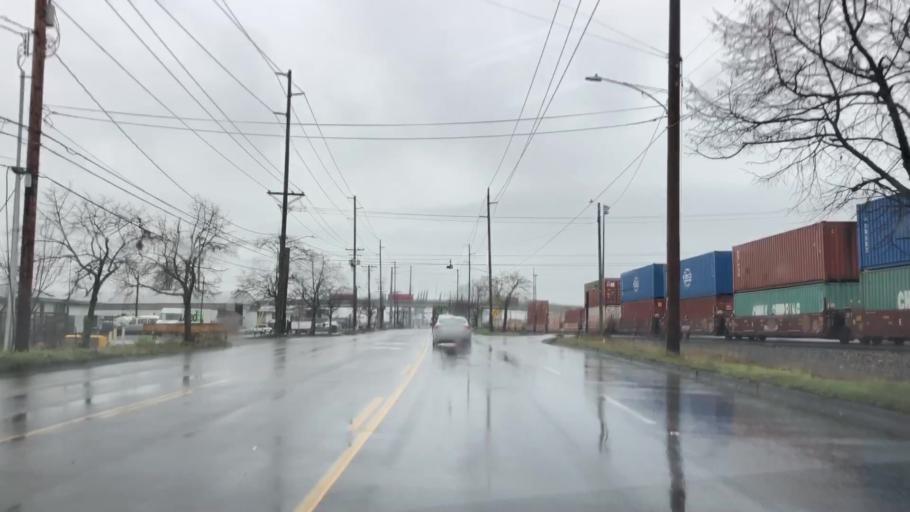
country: US
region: Washington
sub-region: Pierce County
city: Tacoma
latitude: 47.2526
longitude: -122.4023
